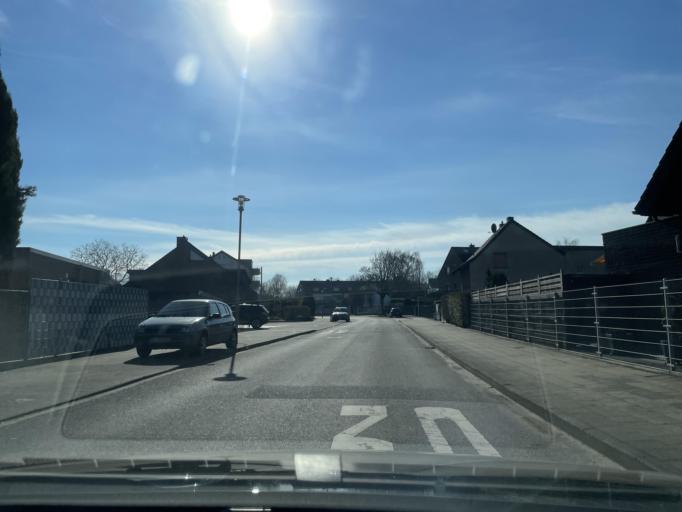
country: DE
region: North Rhine-Westphalia
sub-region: Regierungsbezirk Dusseldorf
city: Monchengladbach
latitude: 51.2263
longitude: 6.4485
